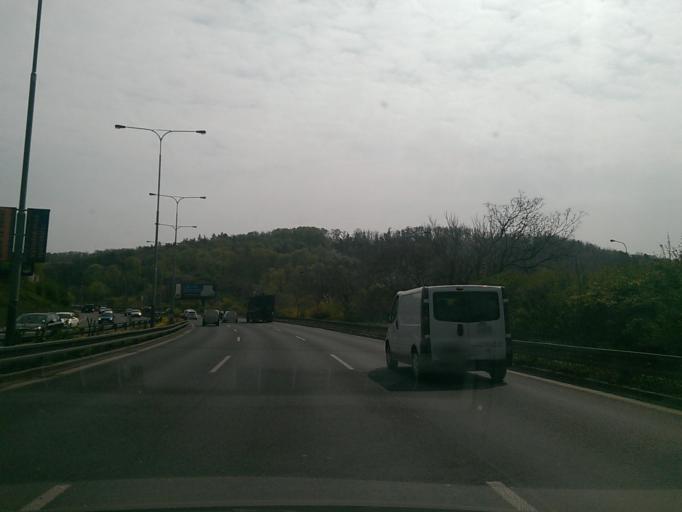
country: CZ
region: Praha
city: Branik
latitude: 50.0331
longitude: 14.4094
